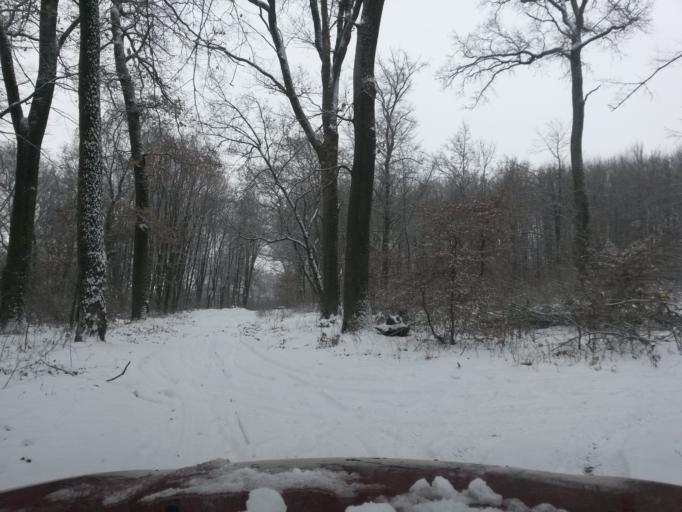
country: SK
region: Kosicky
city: Kosice
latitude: 48.7165
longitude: 21.3294
